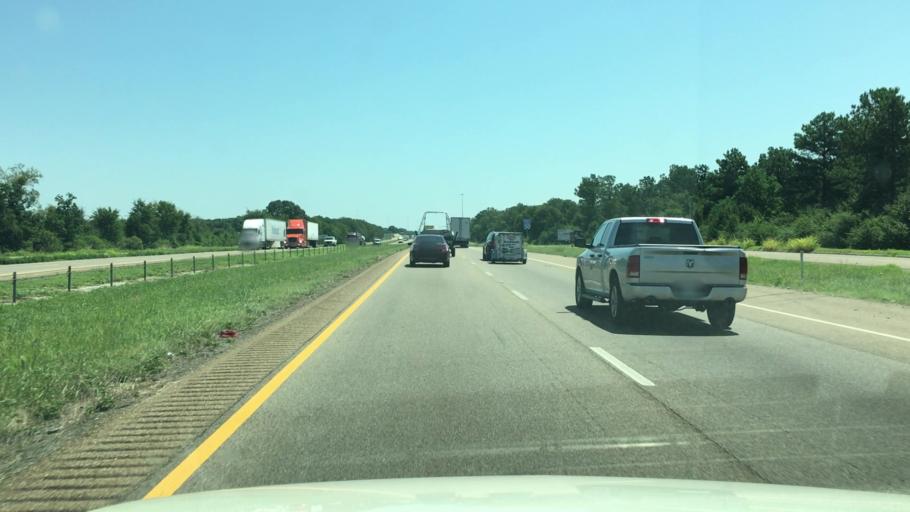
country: US
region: Texas
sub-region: Bowie County
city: Hooks
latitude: 33.4692
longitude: -94.3270
